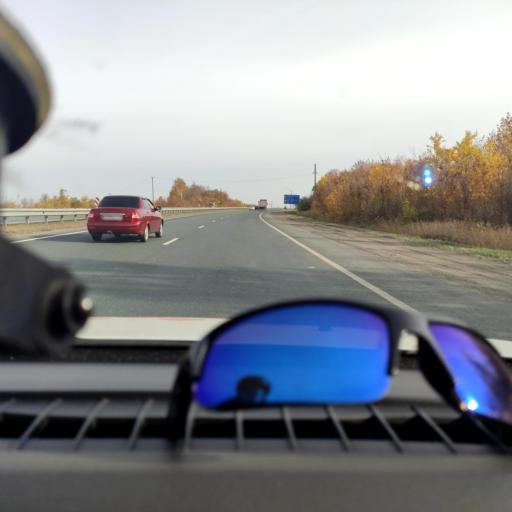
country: RU
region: Samara
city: Novokuybyshevsk
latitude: 53.0006
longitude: 49.9603
